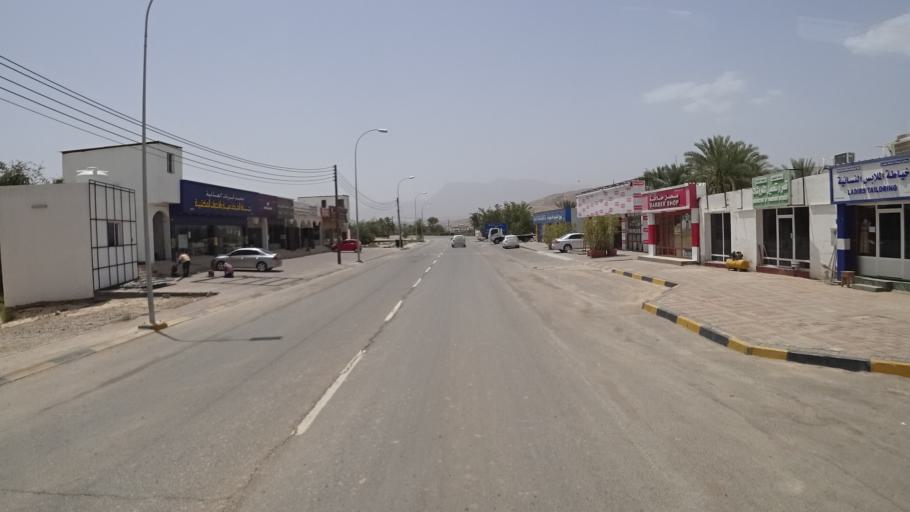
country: OM
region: Muhafazat Masqat
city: Muscat
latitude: 23.2408
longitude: 58.9022
